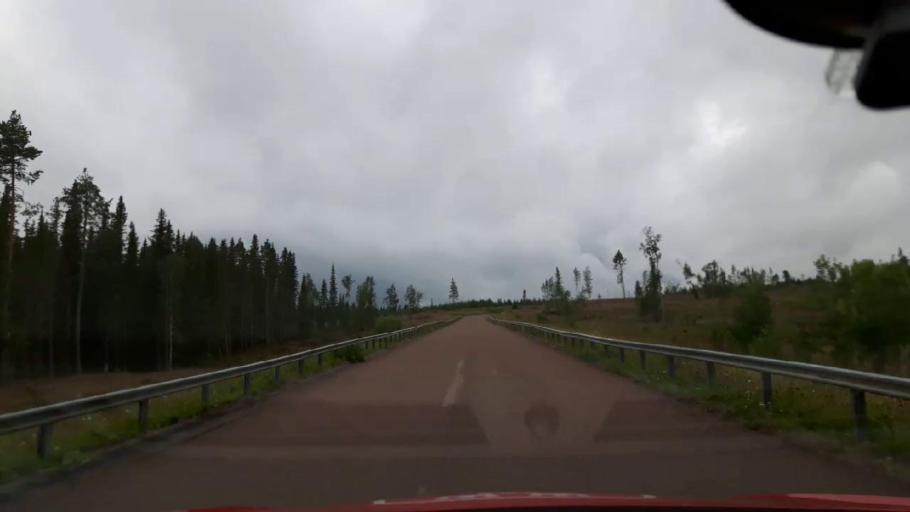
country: SE
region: Jaemtland
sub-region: Krokoms Kommun
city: Valla
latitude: 63.3753
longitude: 13.7573
